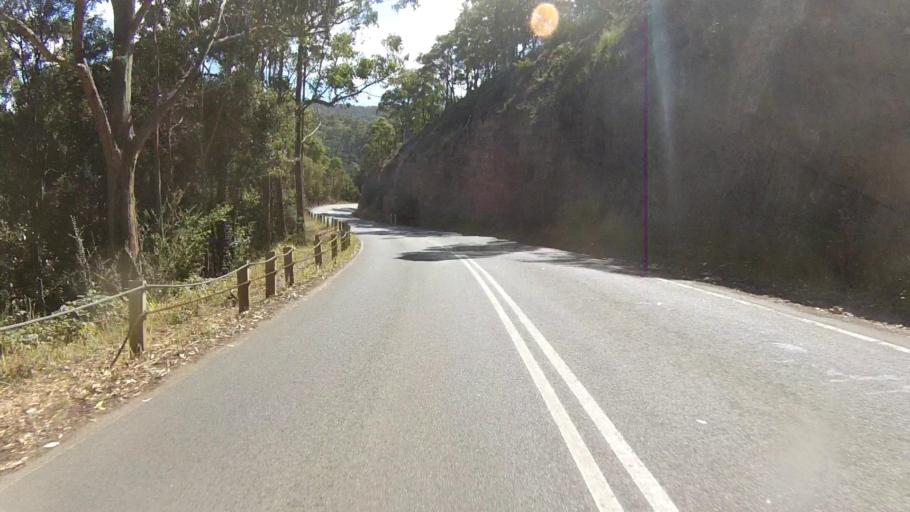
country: AU
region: Tasmania
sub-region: Derwent Valley
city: New Norfolk
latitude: -42.6847
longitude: 146.7274
